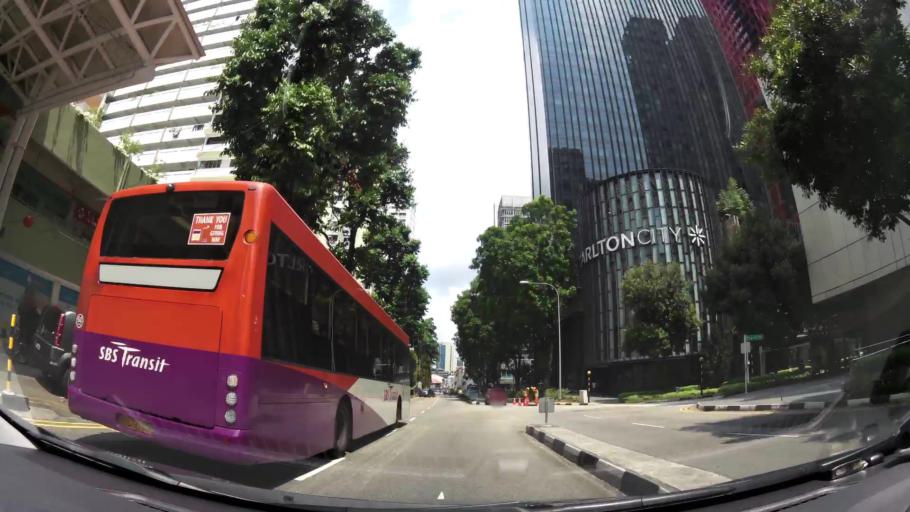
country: SG
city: Singapore
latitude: 1.2754
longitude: 103.8432
